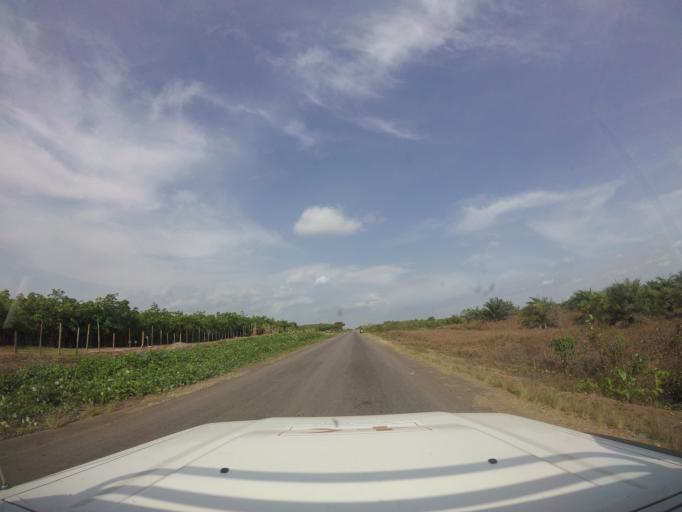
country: LR
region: Bomi
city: Tubmanburg
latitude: 6.7294
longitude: -11.0191
